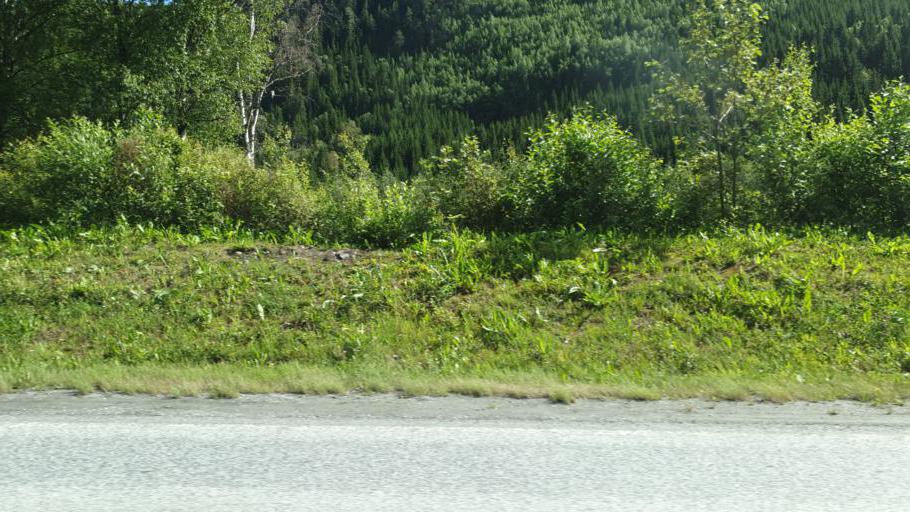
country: NO
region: Sor-Trondelag
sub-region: Midtre Gauldal
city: Storen
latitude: 62.9999
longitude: 10.2384
